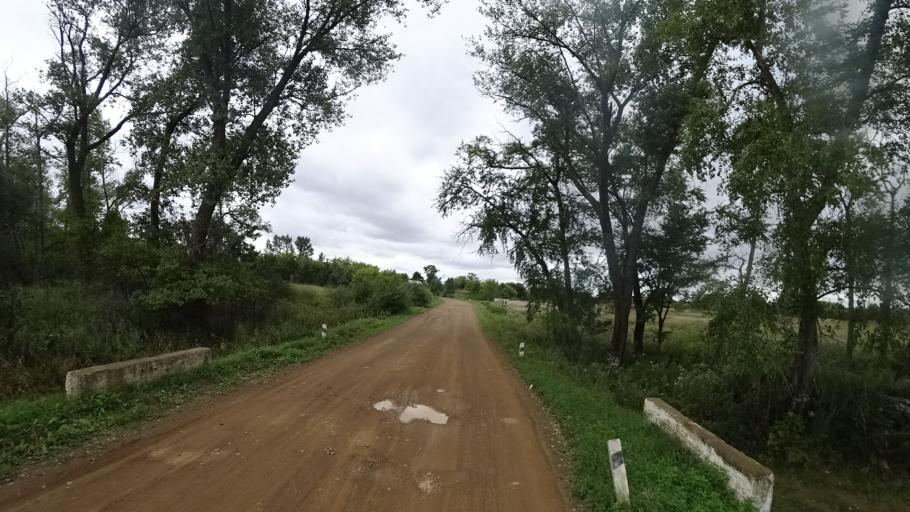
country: RU
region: Primorskiy
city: Chernigovka
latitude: 44.4444
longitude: 132.5730
